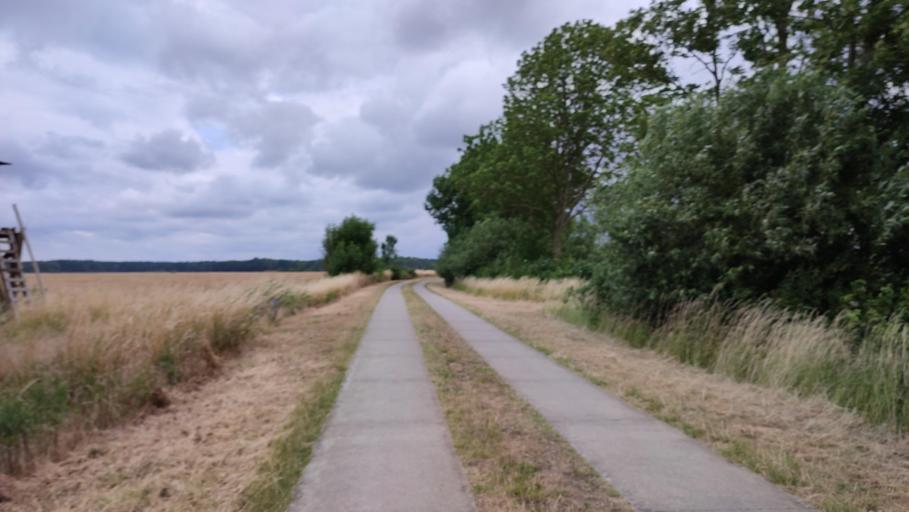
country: DE
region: Lower Saxony
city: Hitzacker
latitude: 53.1736
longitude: 11.1014
